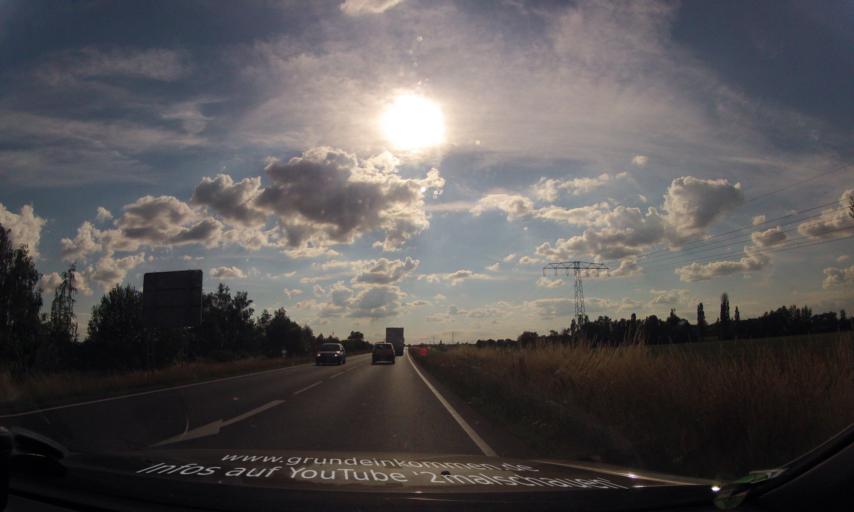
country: DE
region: Saxony
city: Borsdorf
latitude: 51.3549
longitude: 12.5384
